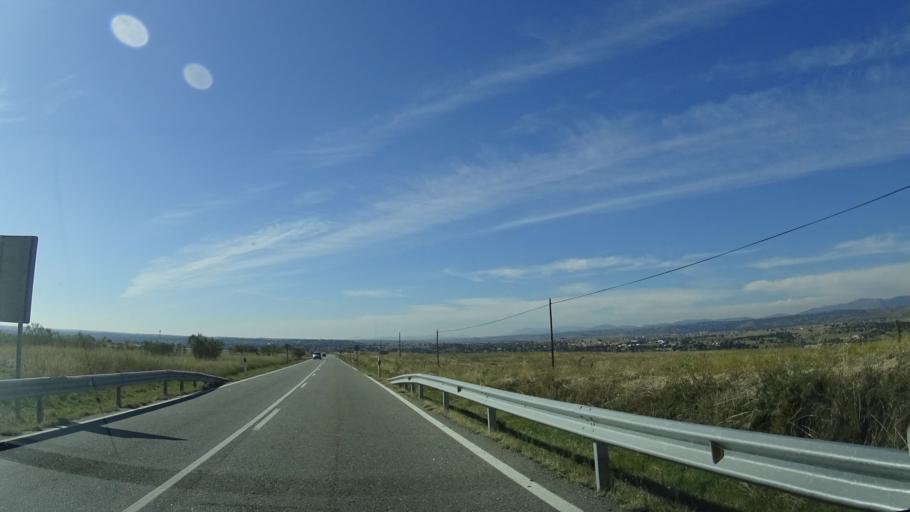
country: ES
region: Madrid
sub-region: Provincia de Madrid
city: Las Rozas de Madrid
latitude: 40.4922
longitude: -3.9158
